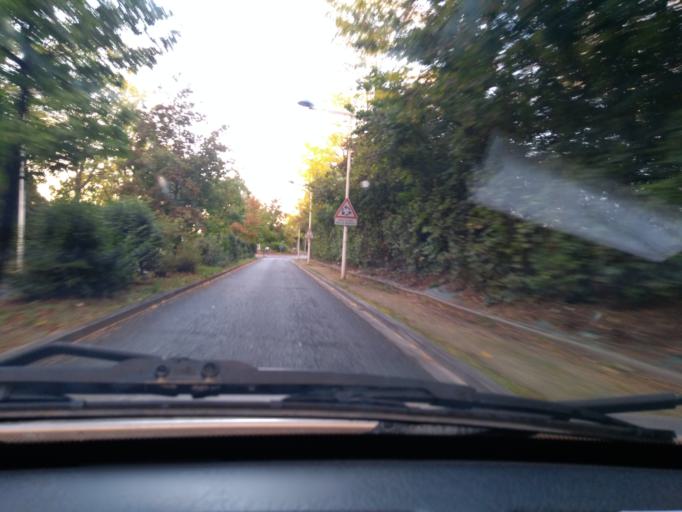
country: FR
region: Poitou-Charentes
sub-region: Departement de la Charente
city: Angouleme
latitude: 45.6424
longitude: 0.1419
